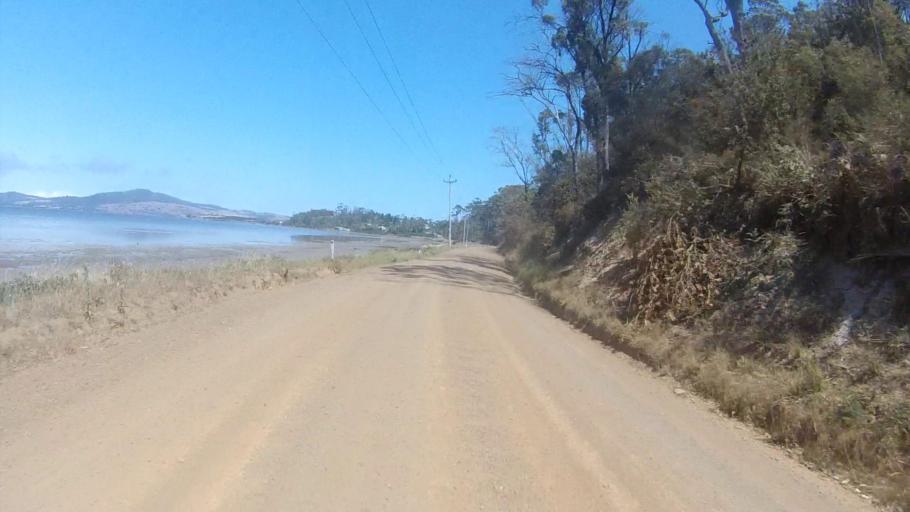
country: AU
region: Tasmania
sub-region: Sorell
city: Sorell
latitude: -42.8475
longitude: 147.8423
